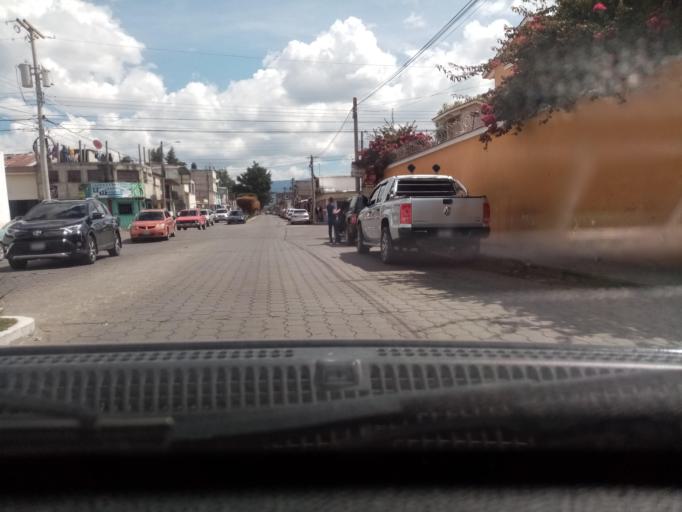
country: GT
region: Quetzaltenango
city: Quetzaltenango
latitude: 14.8488
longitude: -91.5269
